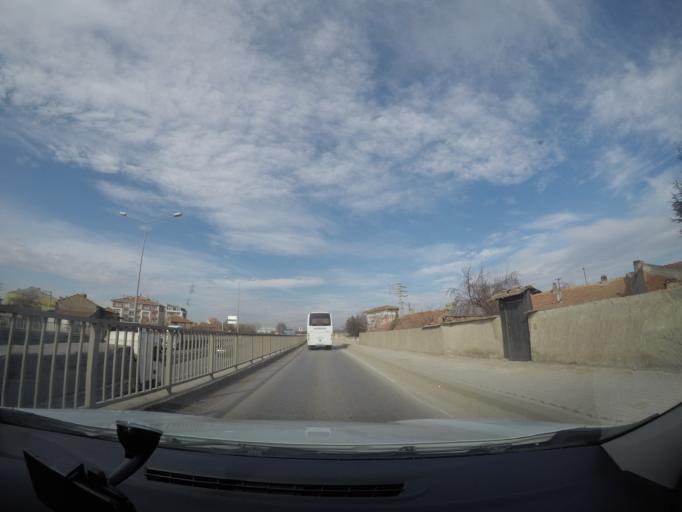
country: TR
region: Eskisehir
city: Eskisehir
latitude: 39.7963
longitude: 30.5313
